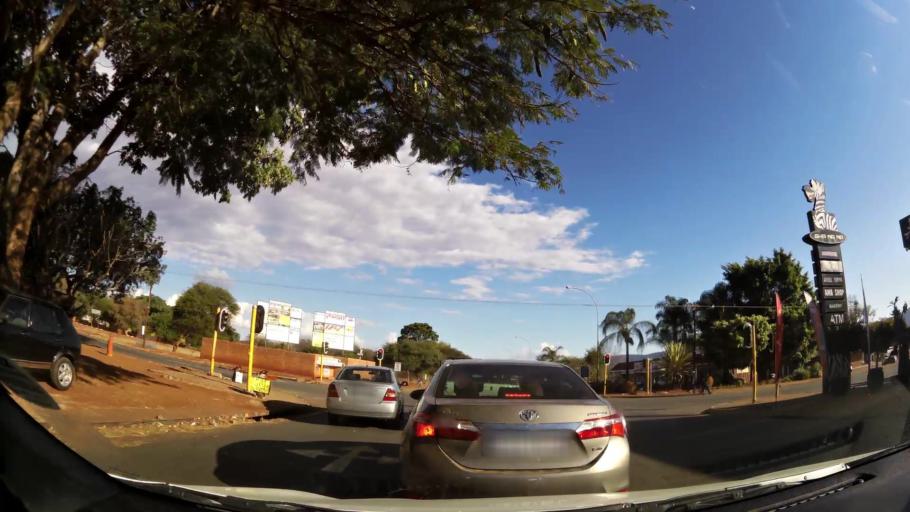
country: ZA
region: Limpopo
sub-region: Waterberg District Municipality
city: Mokopane
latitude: -24.1927
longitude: 29.0051
